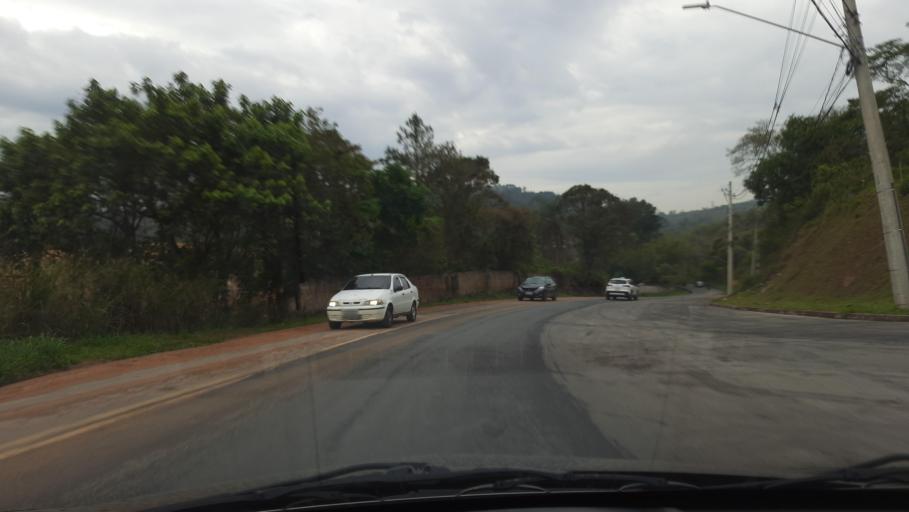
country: BR
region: Sao Paulo
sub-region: Caieiras
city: Caieiras
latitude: -23.3749
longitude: -46.6992
